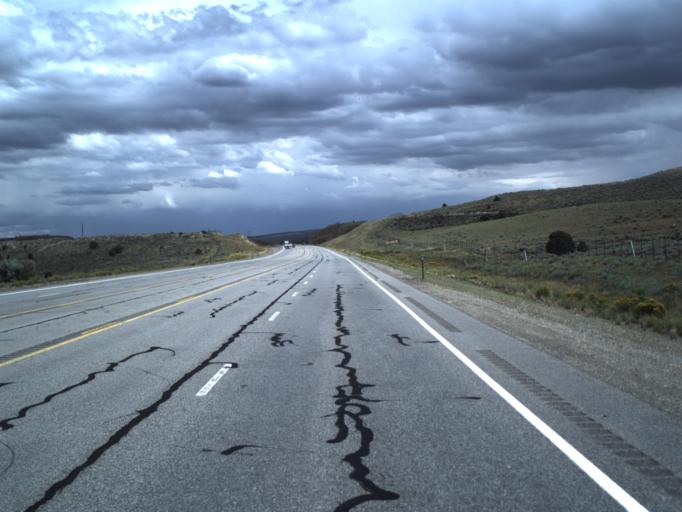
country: US
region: Utah
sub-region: Carbon County
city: Helper
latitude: 39.8348
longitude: -110.9745
